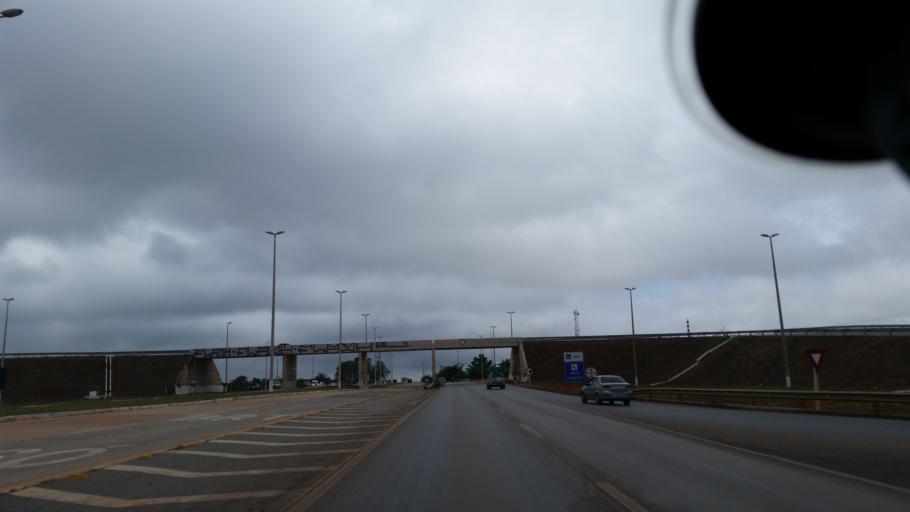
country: BR
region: Federal District
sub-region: Brasilia
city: Brasilia
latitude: -15.9798
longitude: -47.9894
